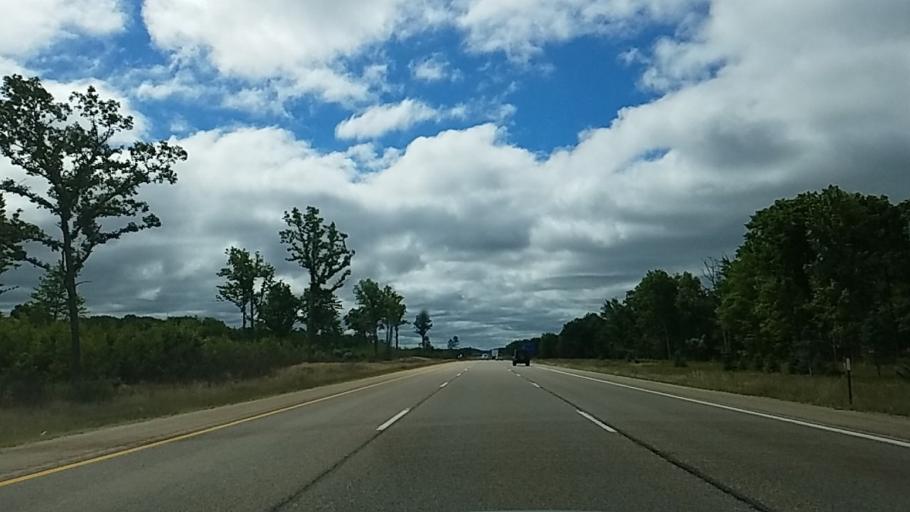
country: US
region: Michigan
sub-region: Crawford County
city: Grayling
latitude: 44.6137
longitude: -84.7090
